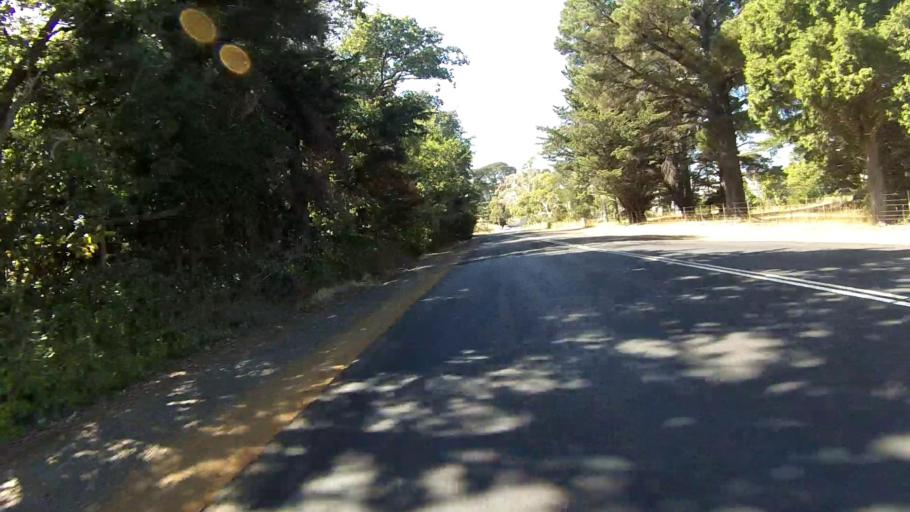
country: AU
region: Tasmania
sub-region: Sorell
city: Sorell
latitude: -42.4981
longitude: 147.9221
